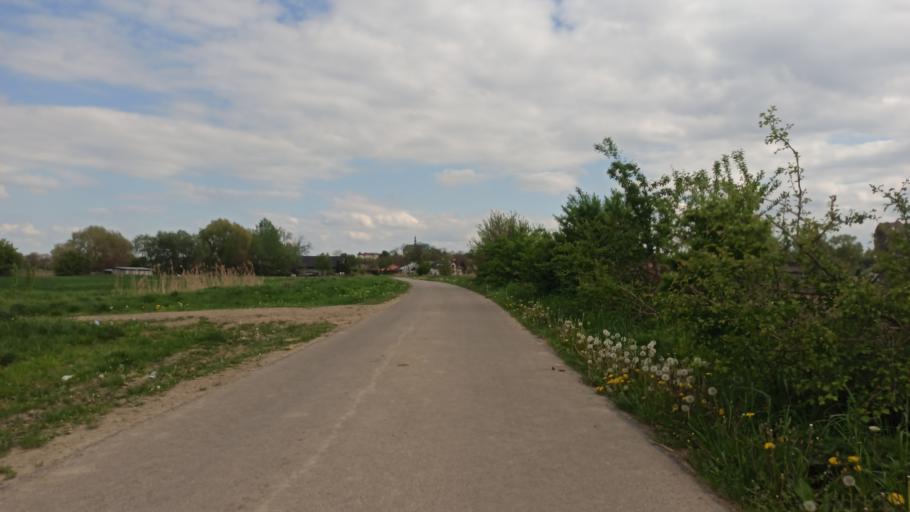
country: PL
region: Subcarpathian Voivodeship
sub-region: Powiat jaroslawski
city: Radymno
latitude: 49.9594
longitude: 22.8110
